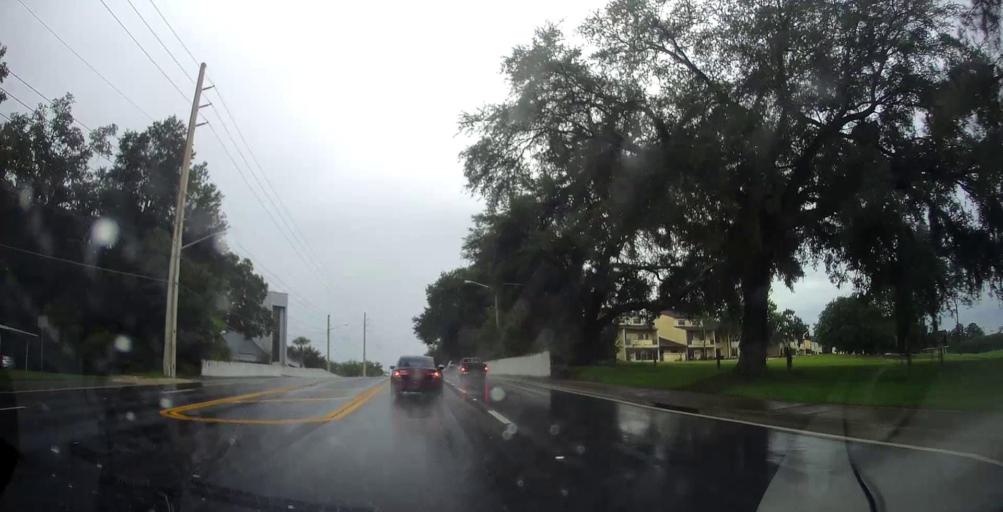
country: US
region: Florida
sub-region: Marion County
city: Ocala
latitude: 29.1885
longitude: -82.0869
